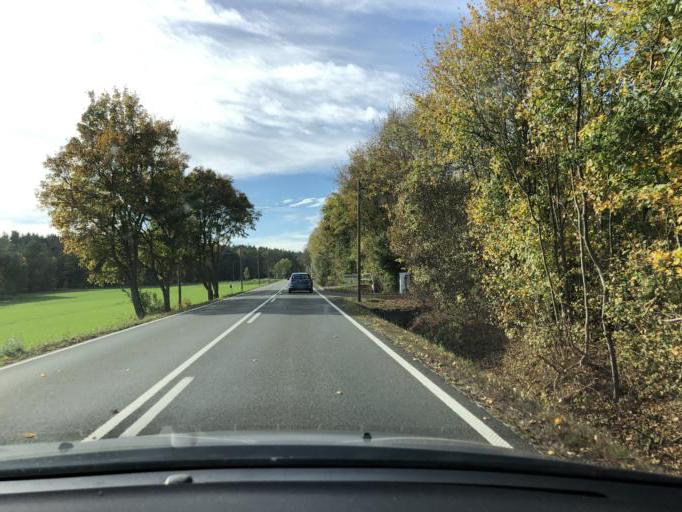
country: DE
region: Thuringia
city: Zedlitz
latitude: 50.8299
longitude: 12.0163
